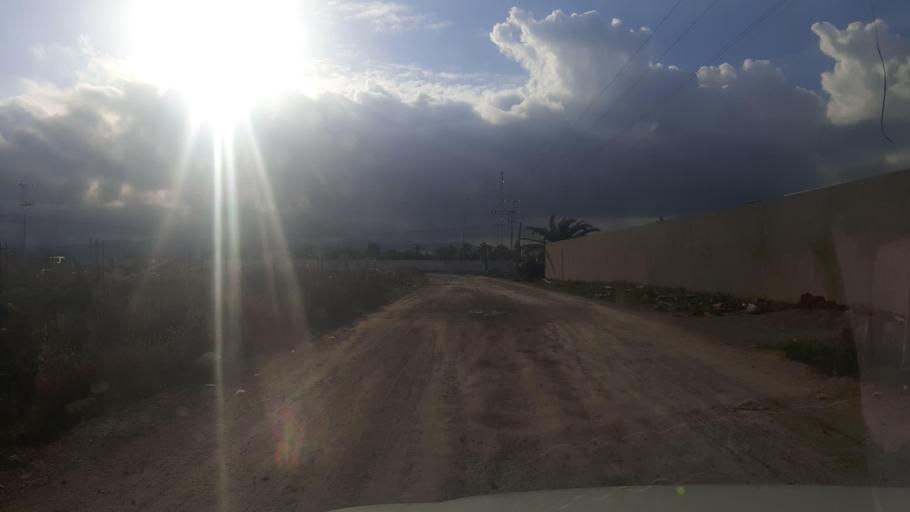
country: TN
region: Nabul
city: Manzil Bu Zalafah
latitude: 36.7109
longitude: 10.4835
